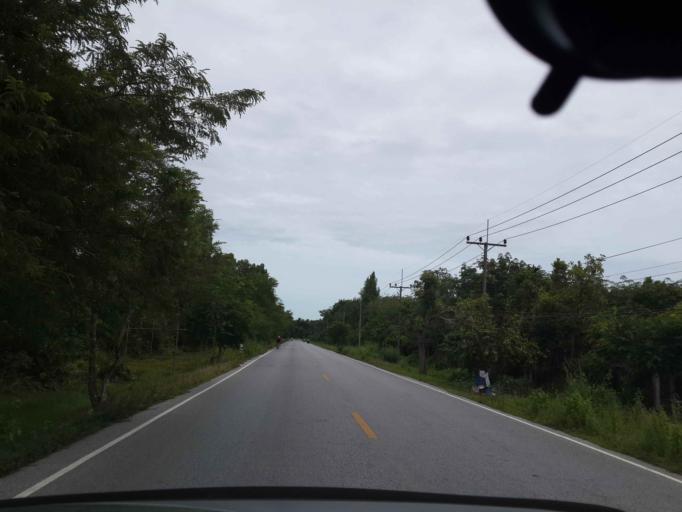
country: TH
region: Narathiwat
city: Yi-ngo
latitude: 6.3629
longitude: 101.6647
